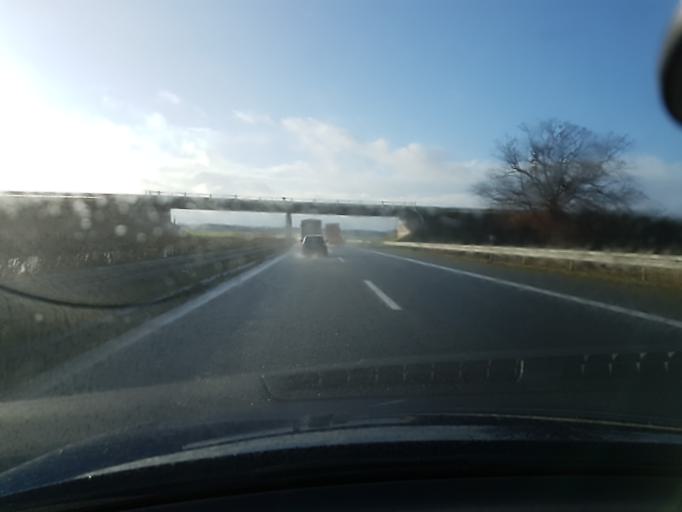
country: DE
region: Mecklenburg-Vorpommern
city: Tessin
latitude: 54.0195
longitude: 12.5612
